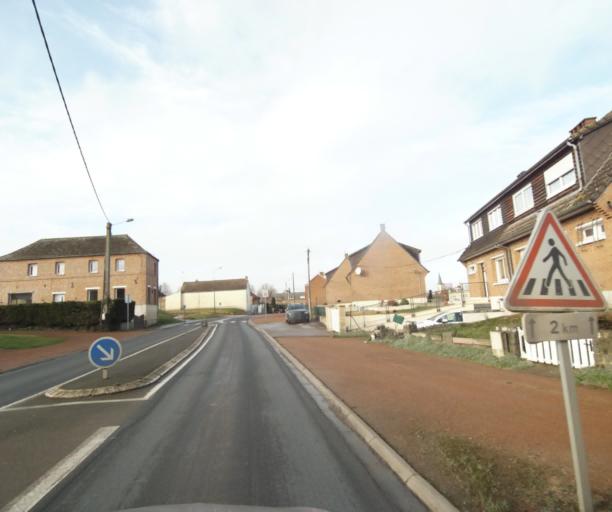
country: FR
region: Nord-Pas-de-Calais
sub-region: Departement du Nord
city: Vendegies-sur-Ecaillon
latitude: 50.2647
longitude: 3.4807
